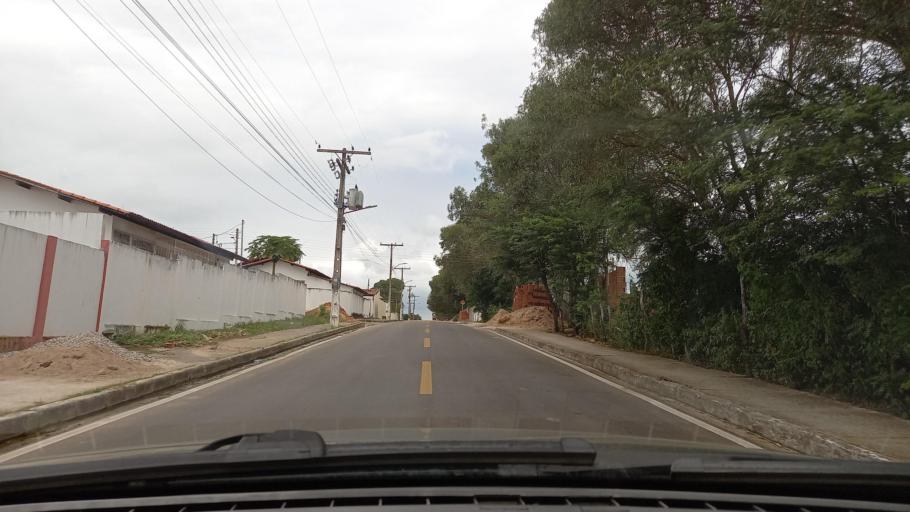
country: BR
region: Sergipe
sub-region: Caninde De Sao Francisco
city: Caninde de Sao Francisco
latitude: -9.6148
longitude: -37.7671
